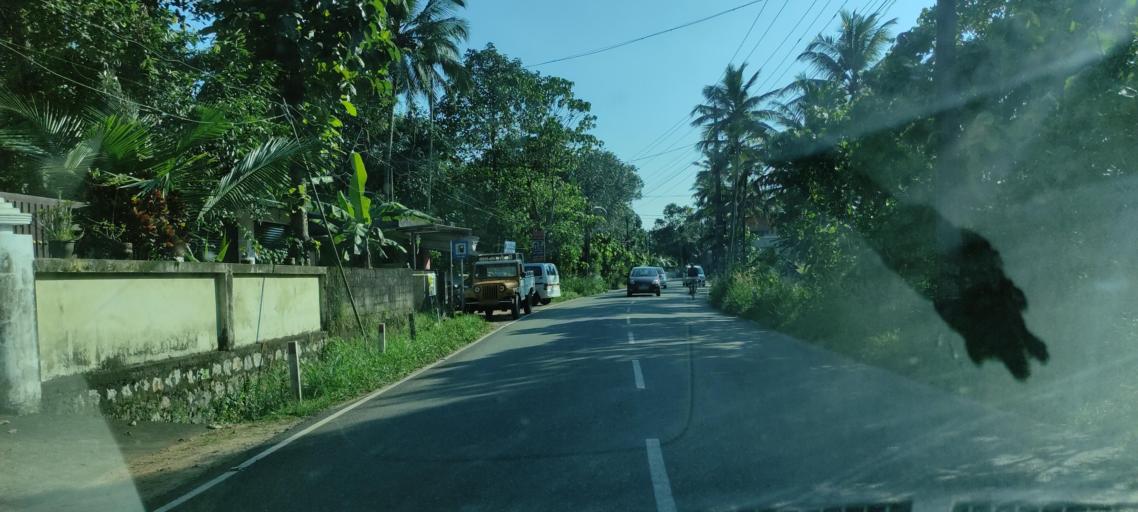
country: IN
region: Kerala
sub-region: Pattanamtitta
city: Adur
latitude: 9.2029
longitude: 76.7450
